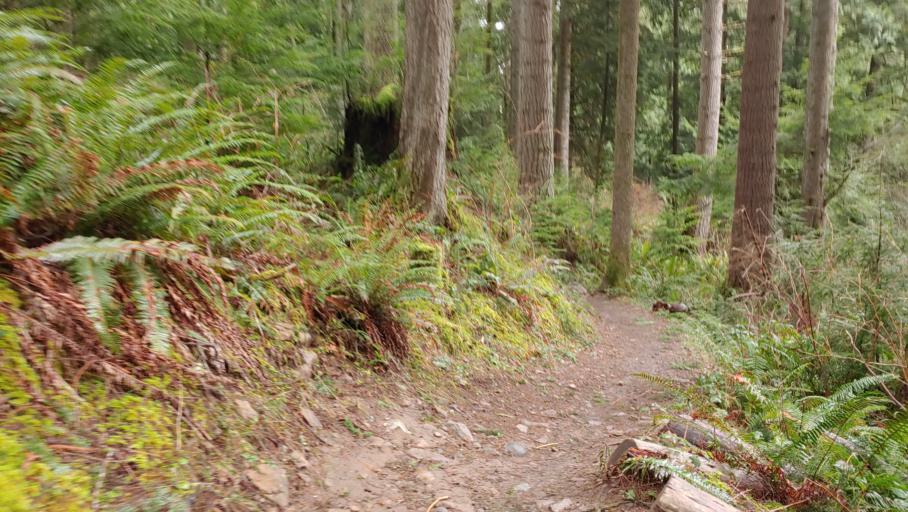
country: US
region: Washington
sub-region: King County
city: Hobart
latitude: 47.4680
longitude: -121.9293
